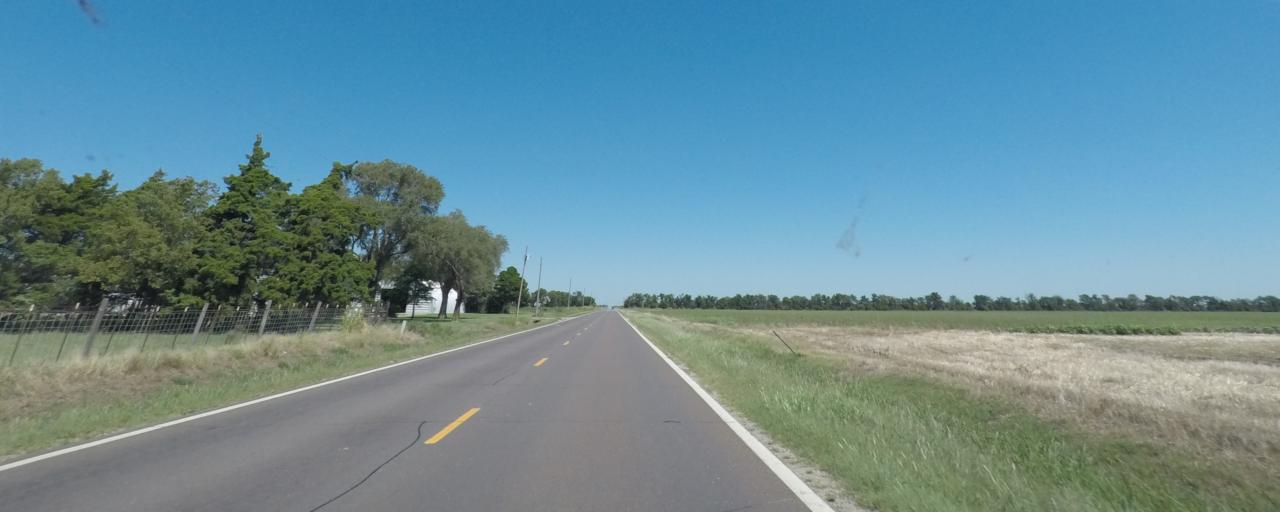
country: US
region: Kansas
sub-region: Sumner County
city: Wellington
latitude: 37.1910
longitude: -97.4022
